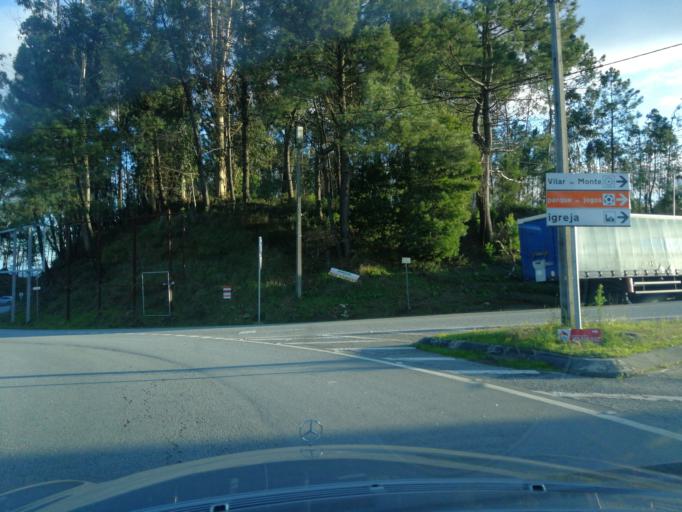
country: PT
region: Braga
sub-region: Barcelos
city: Vila Frescainha
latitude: 41.5623
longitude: -8.6588
